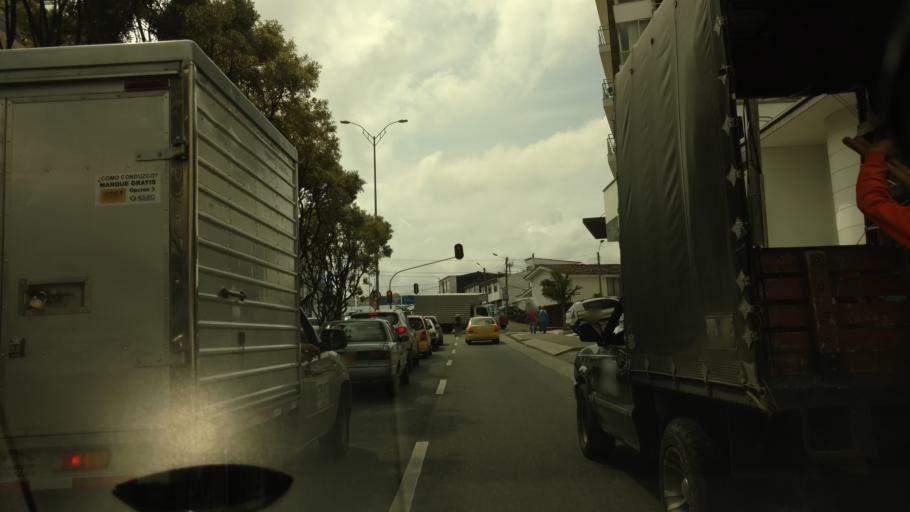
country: CO
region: Caldas
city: Villamaria
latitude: 5.0518
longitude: -75.4843
